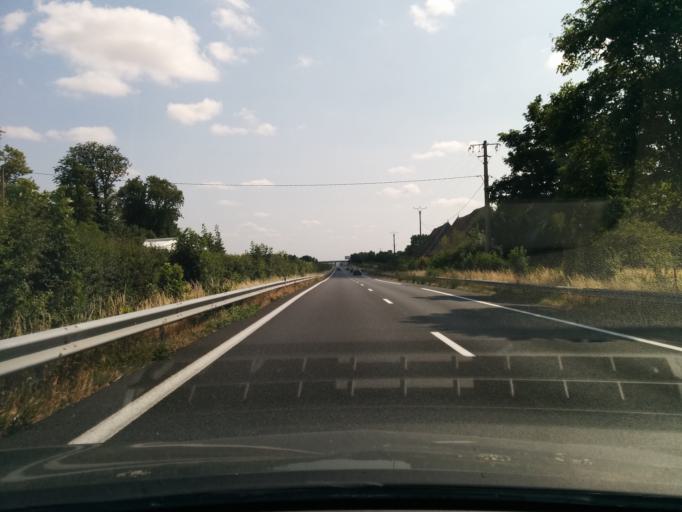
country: FR
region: Centre
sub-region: Departement de l'Indre
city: Montierchaume
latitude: 46.9576
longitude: 1.7582
